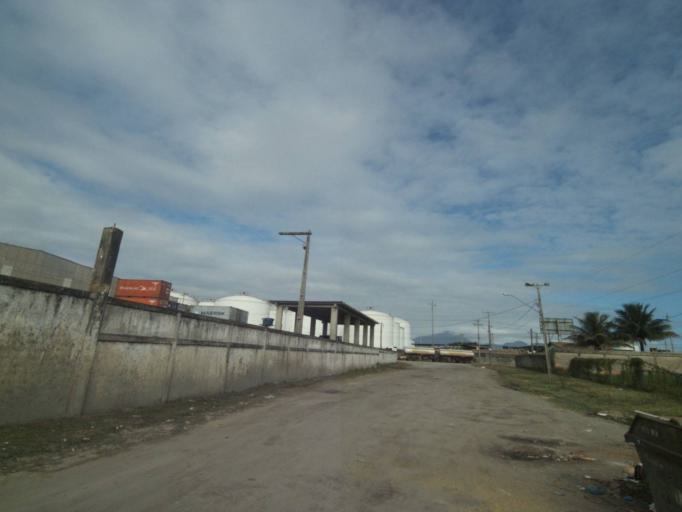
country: BR
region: Parana
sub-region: Paranagua
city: Paranagua
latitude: -25.5086
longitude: -48.5311
